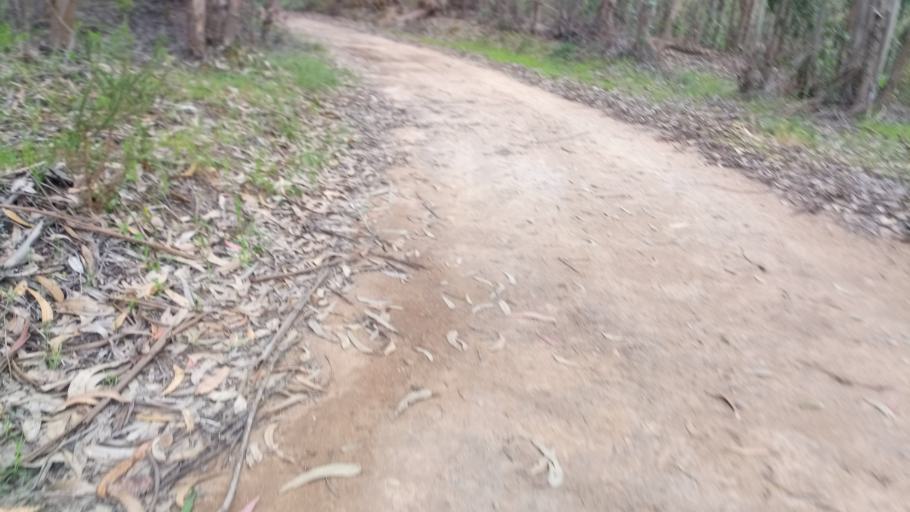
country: PT
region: Leiria
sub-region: Obidos
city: Obidos
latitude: 39.3884
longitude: -9.2106
